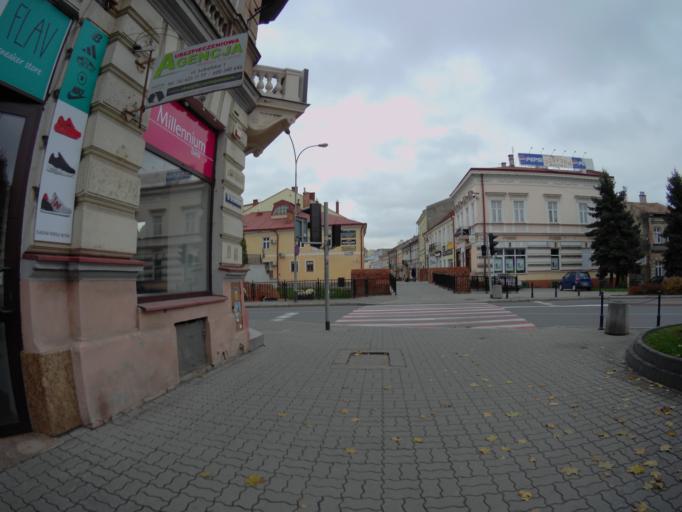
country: PL
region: Subcarpathian Voivodeship
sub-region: Powiat jaroslawski
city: Jaroslaw
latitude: 50.0171
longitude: 22.6811
